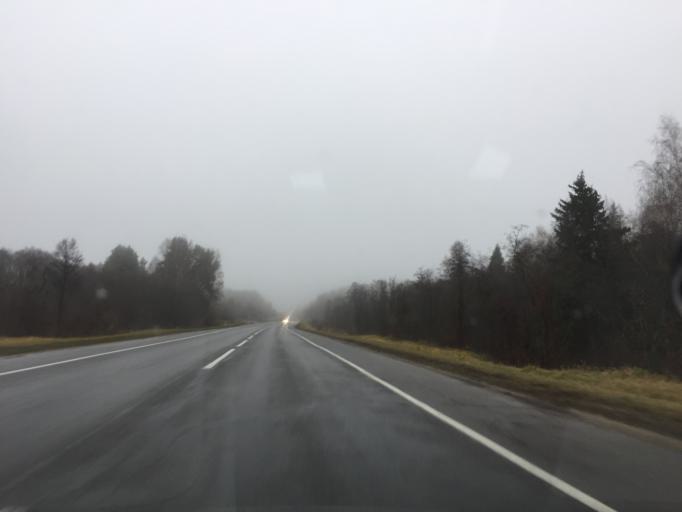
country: BY
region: Mogilev
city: Palykavichy Pyershyya
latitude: 54.0527
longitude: 30.4622
